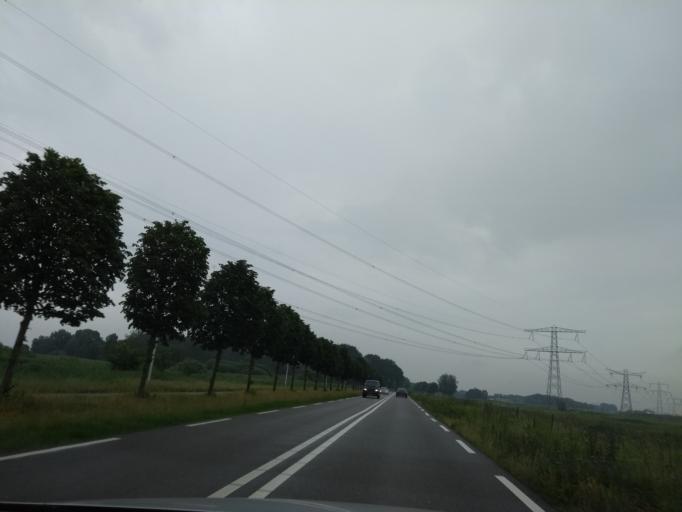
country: NL
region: North Holland
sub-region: Gemeente Weesp
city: Weesp
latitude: 52.3324
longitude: 5.0396
